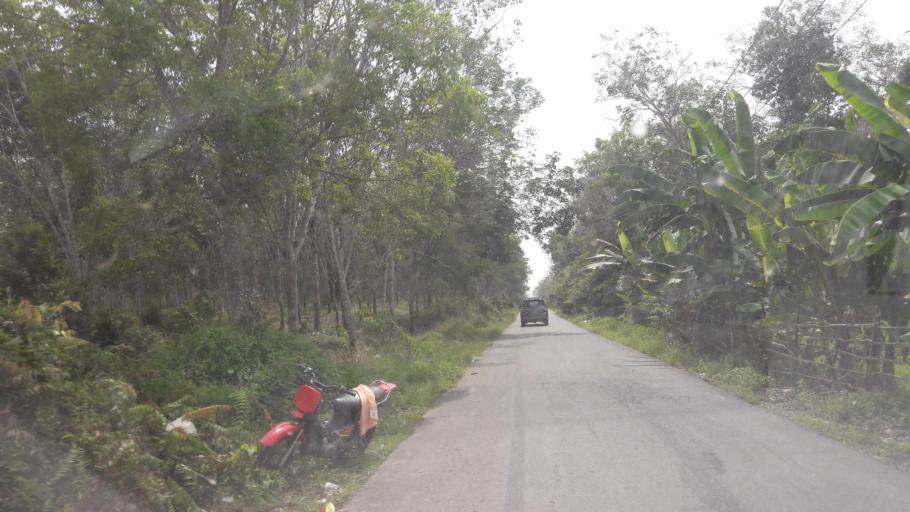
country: ID
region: South Sumatra
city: Gunungmenang
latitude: -3.1596
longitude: 104.1155
